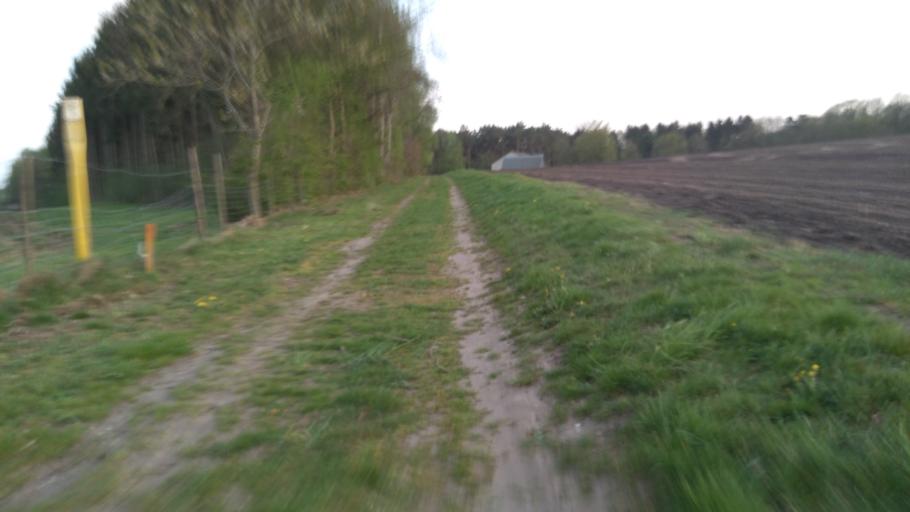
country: DE
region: Lower Saxony
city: Bliedersdorf
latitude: 53.4852
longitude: 9.5575
